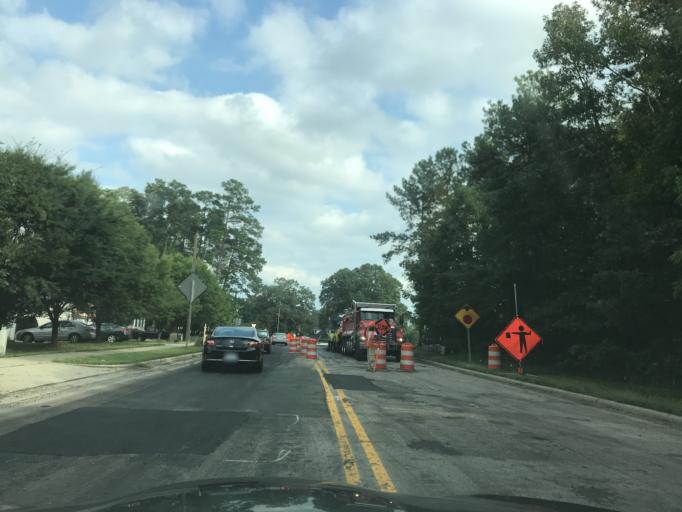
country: US
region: North Carolina
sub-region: Durham County
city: Durham
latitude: 35.9029
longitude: -78.9289
